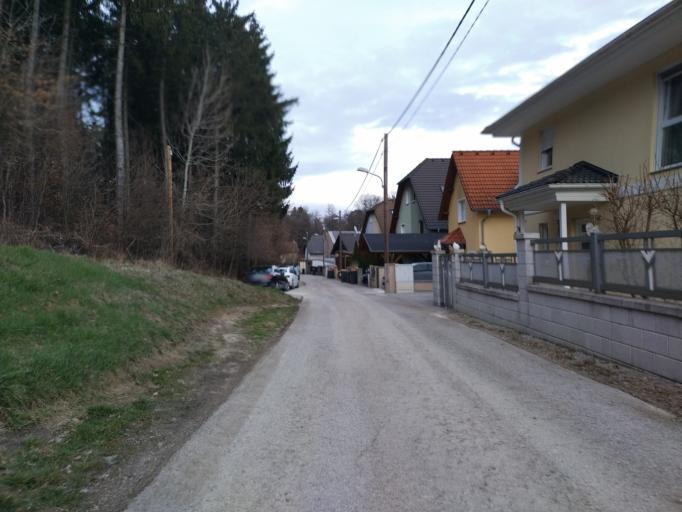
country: AT
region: Lower Austria
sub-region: Politischer Bezirk Wien-Umgebung
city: Gablitz
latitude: 48.2328
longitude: 16.1260
